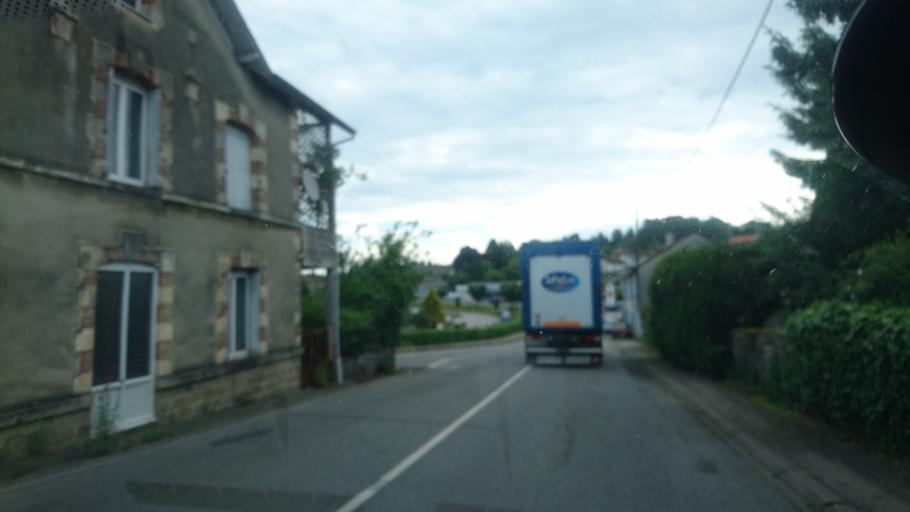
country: FR
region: Limousin
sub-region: Departement de la Haute-Vienne
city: Chateauneuf-la-Foret
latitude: 45.7091
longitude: 1.5971
